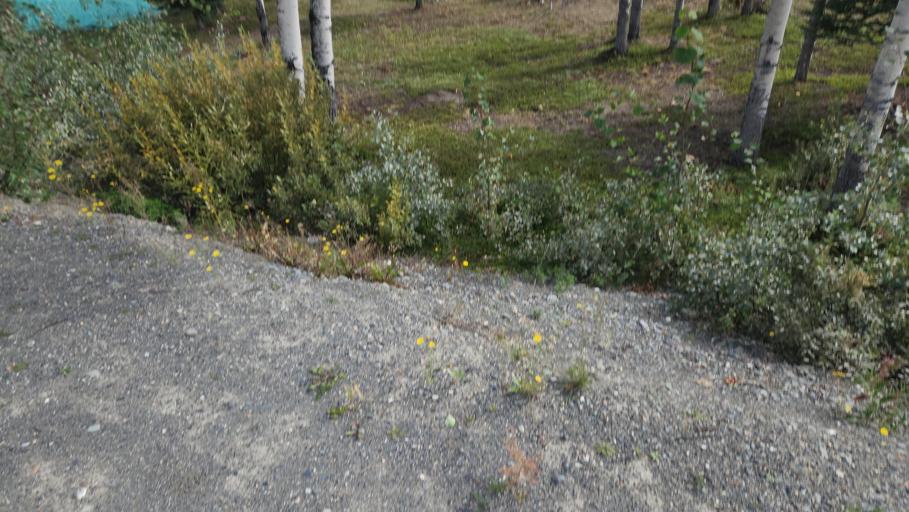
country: CA
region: Yukon
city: Haines Junction
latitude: 60.7618
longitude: -137.5151
